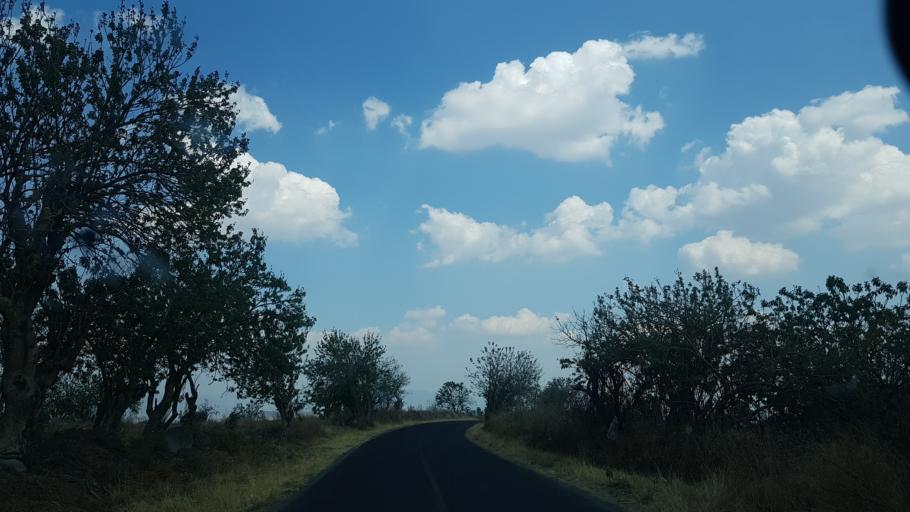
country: MX
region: Puebla
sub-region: Atlixco
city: San Pedro Benito Juarez
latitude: 18.9485
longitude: -98.5396
